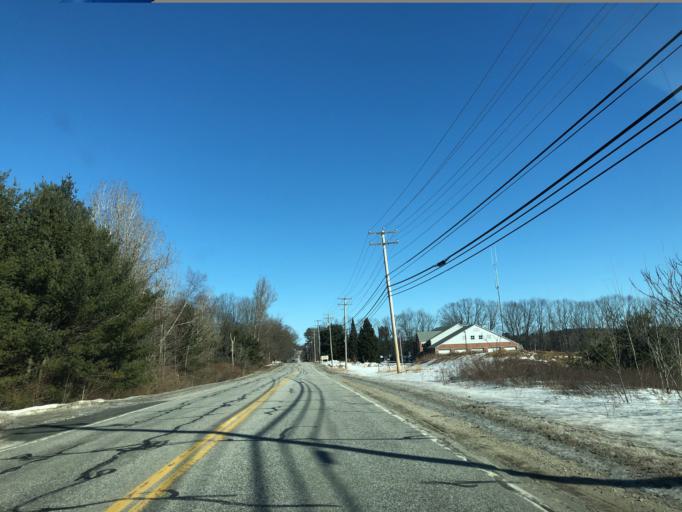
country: US
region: Maine
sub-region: Cumberland County
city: South Windham
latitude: 43.7777
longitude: -70.4166
